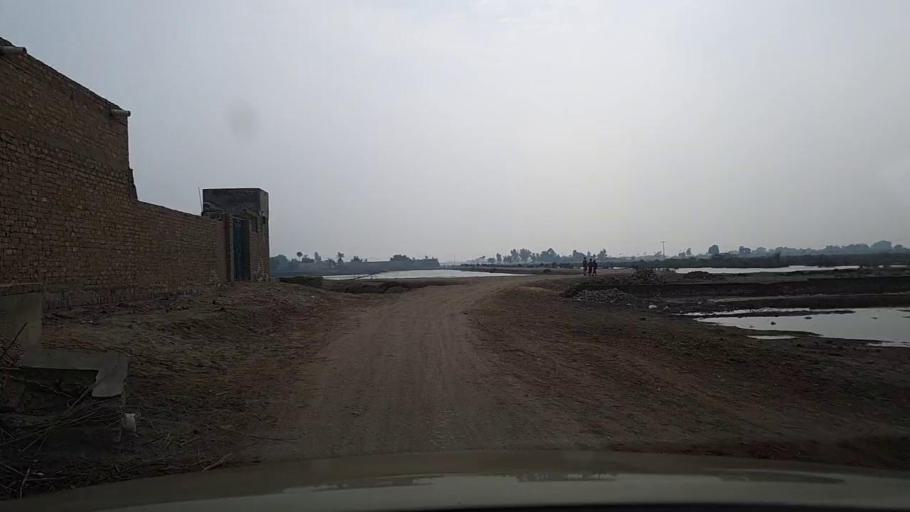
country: PK
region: Sindh
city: Sanghar
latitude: 26.1196
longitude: 68.9166
